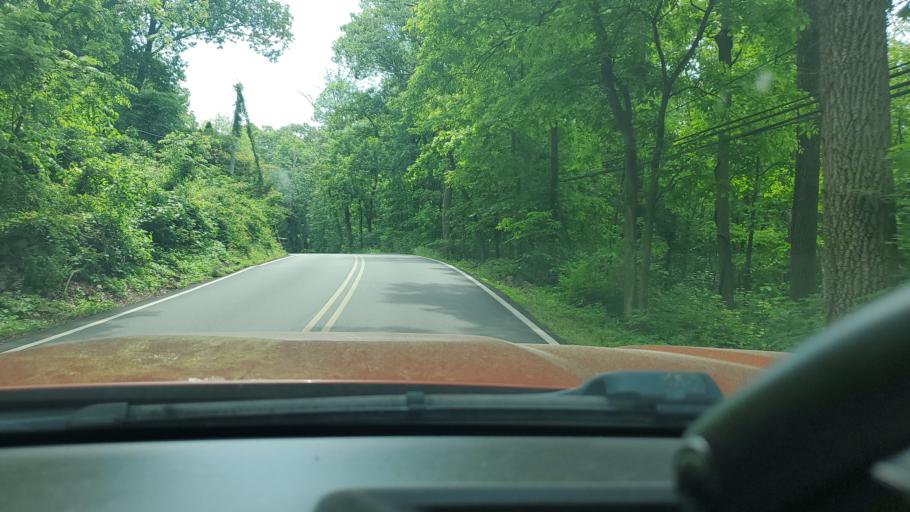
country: US
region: Pennsylvania
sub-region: Montgomery County
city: Red Hill
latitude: 40.3436
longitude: -75.5070
